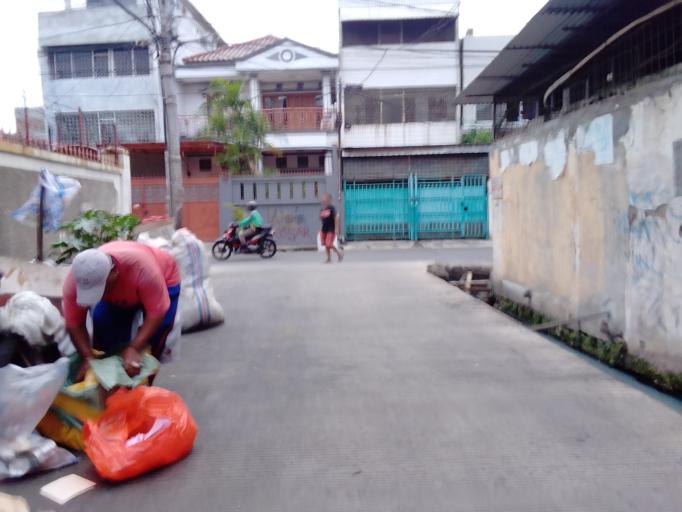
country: ID
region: Jakarta Raya
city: Jakarta
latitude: -6.1567
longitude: 106.8153
